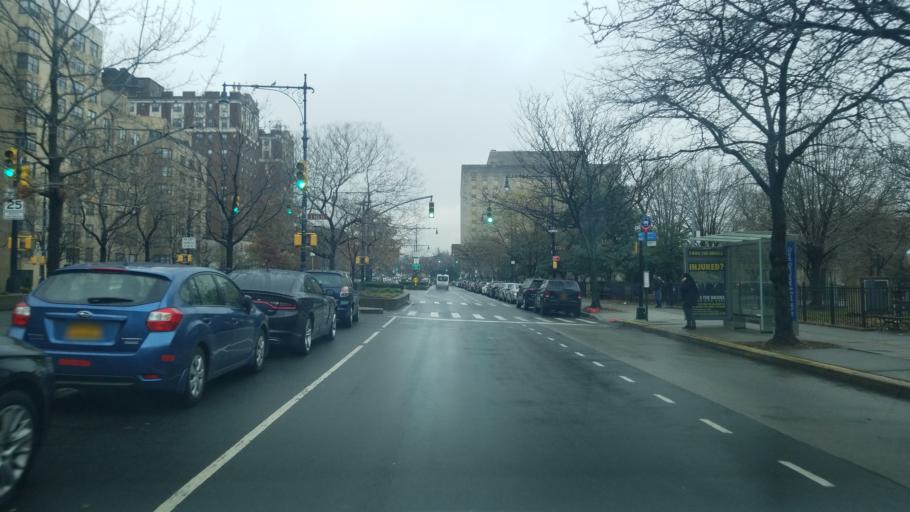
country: US
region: New York
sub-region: New York County
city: Inwood
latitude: 40.8290
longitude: -73.9217
